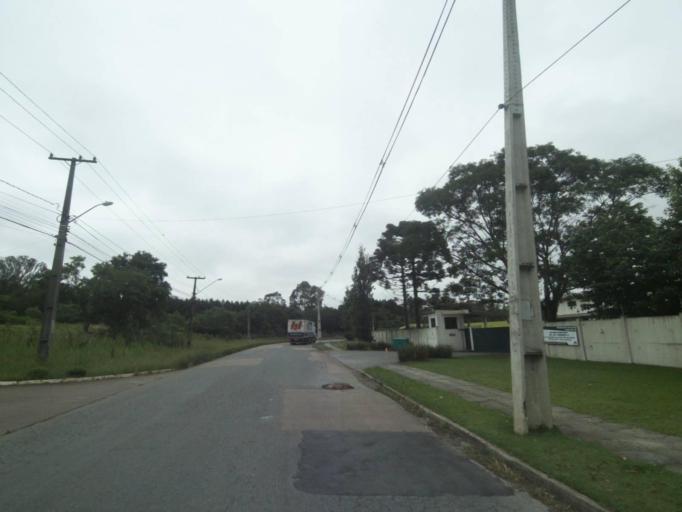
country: BR
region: Parana
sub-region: Araucaria
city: Araucaria
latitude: -25.5429
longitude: -49.3224
